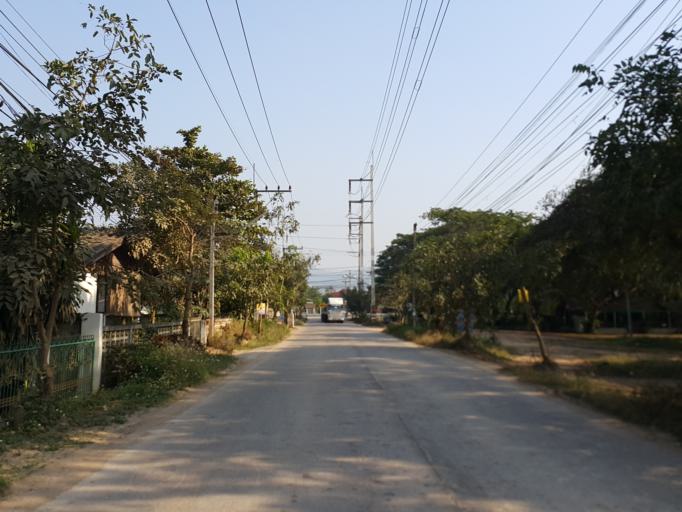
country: TH
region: Lampang
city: Lampang
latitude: 18.3416
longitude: 99.5411
